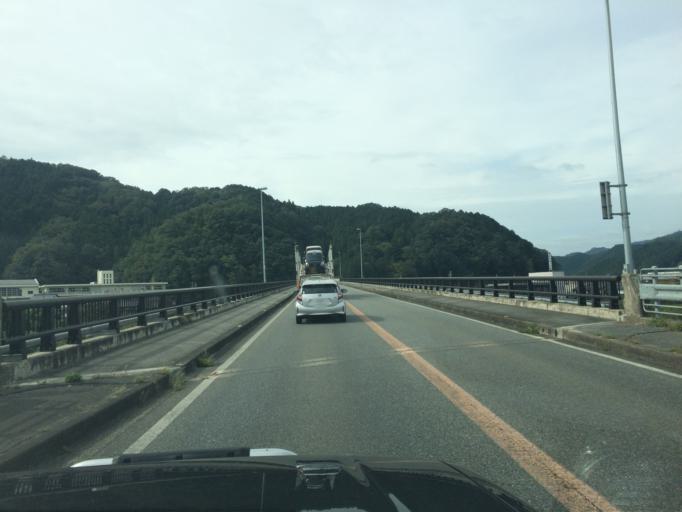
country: JP
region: Hyogo
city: Toyooka
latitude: 35.3342
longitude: 134.8594
